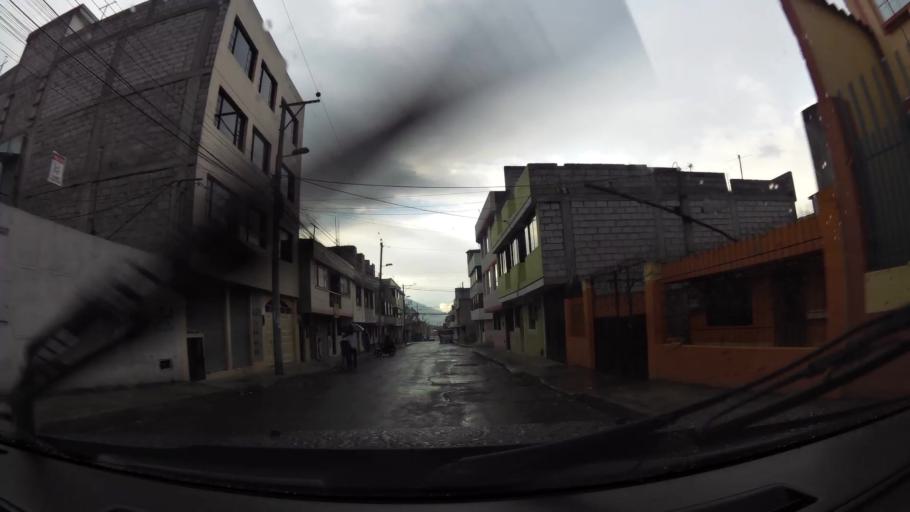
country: EC
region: Pichincha
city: Quito
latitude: -0.3082
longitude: -78.5475
